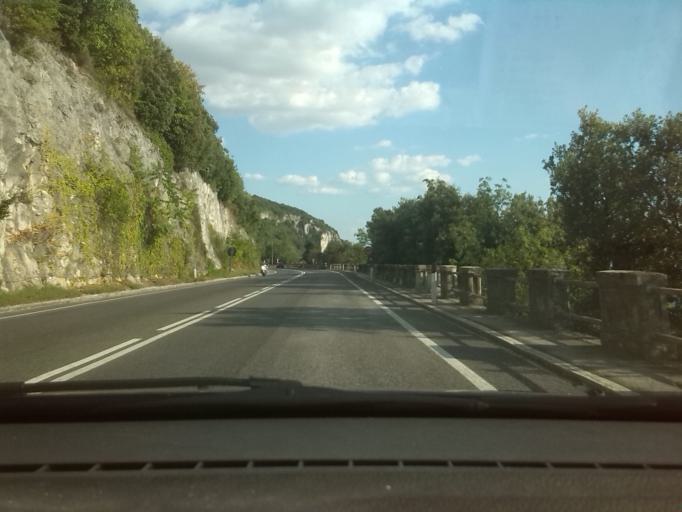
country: IT
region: Friuli Venezia Giulia
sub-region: Provincia di Trieste
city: Aurisina Cave
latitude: 45.7530
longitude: 13.6528
